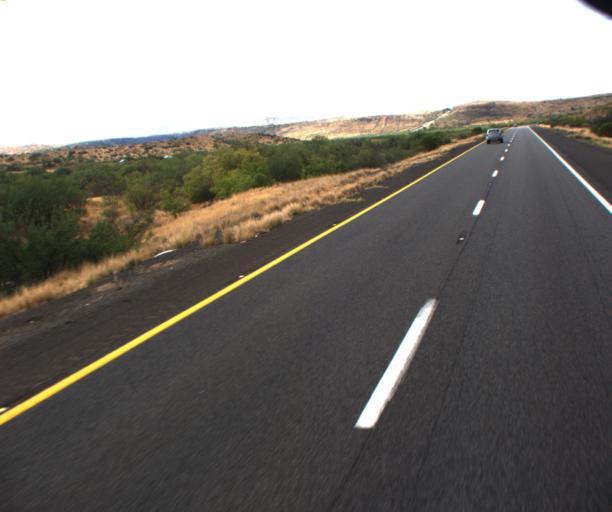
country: US
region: Arizona
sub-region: Yavapai County
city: Cordes Lakes
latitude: 34.2478
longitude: -112.1138
